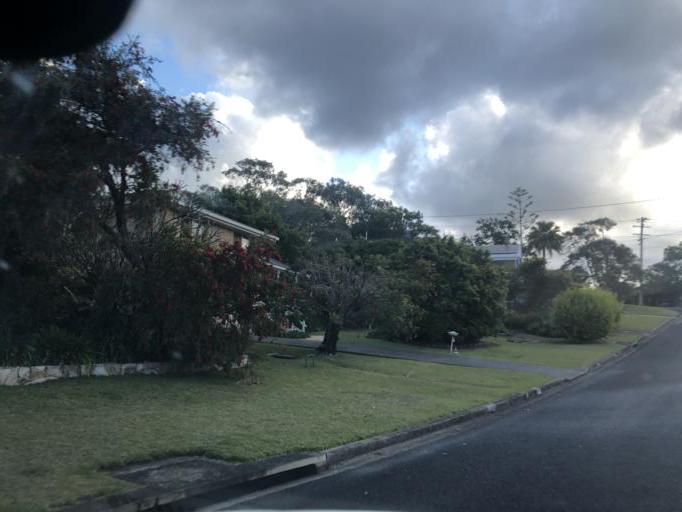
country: AU
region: New South Wales
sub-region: Coffs Harbour
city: Woolgoolga
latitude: -30.0956
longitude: 153.1981
